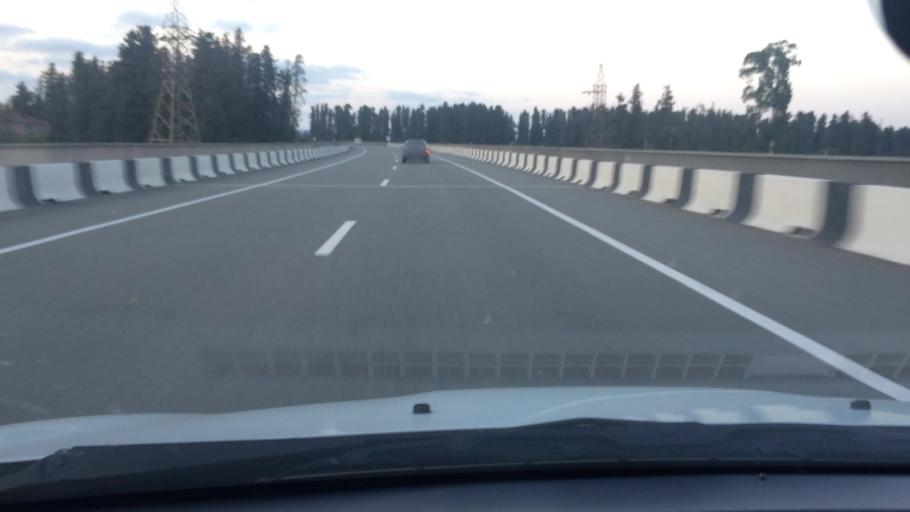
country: GE
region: Ajaria
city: Ochkhamuri
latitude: 41.8524
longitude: 41.8368
